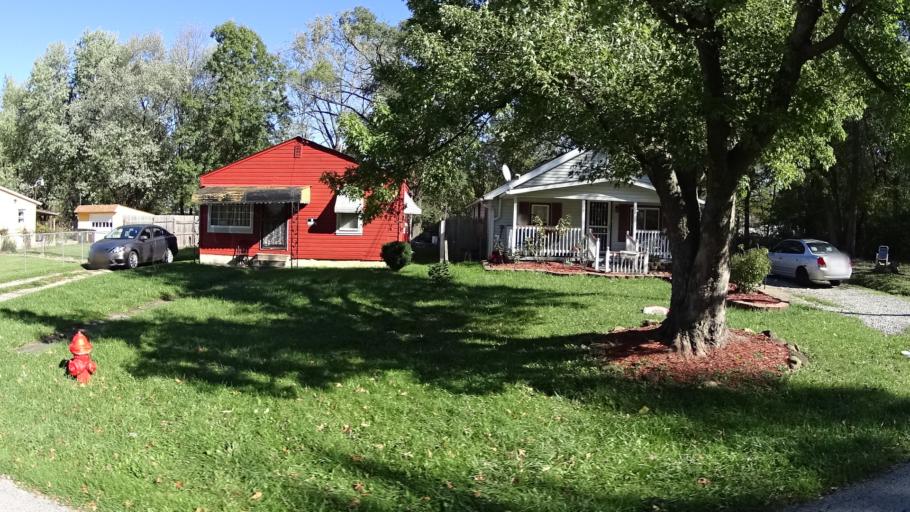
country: US
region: Ohio
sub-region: Lorain County
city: Lorain
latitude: 41.4360
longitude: -82.1520
